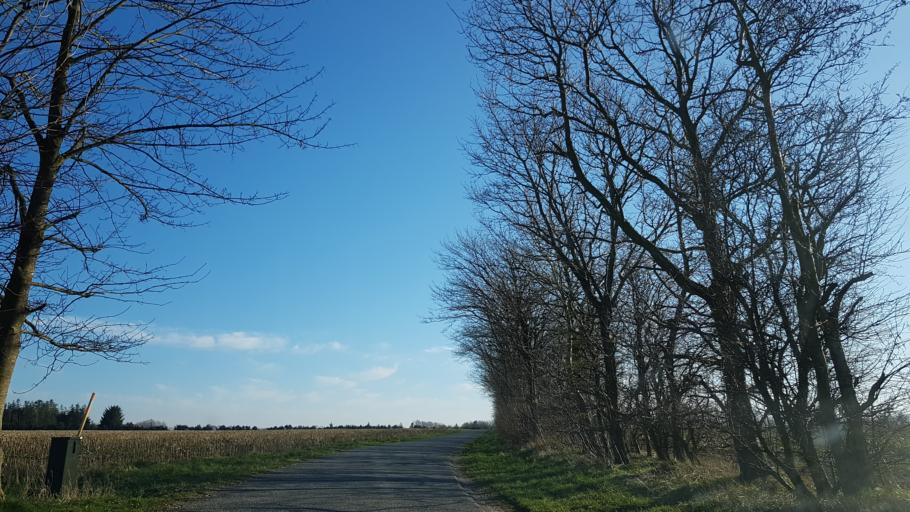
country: DK
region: South Denmark
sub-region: Vejen Kommune
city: Holsted
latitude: 55.4343
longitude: 8.9376
